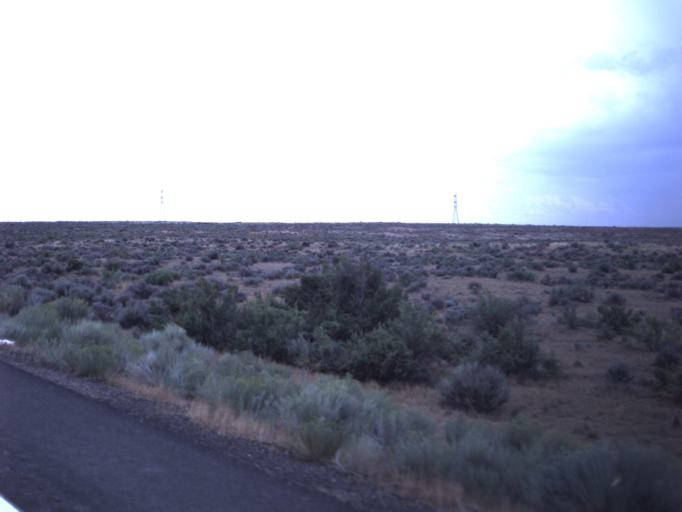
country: US
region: Utah
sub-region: Uintah County
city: Naples
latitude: 40.2394
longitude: -109.4150
